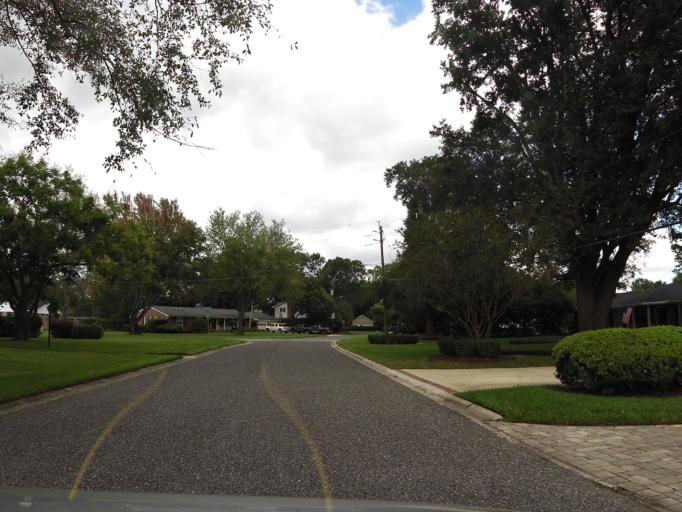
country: US
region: Florida
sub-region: Clay County
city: Bellair-Meadowbrook Terrace
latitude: 30.2569
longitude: -81.7067
